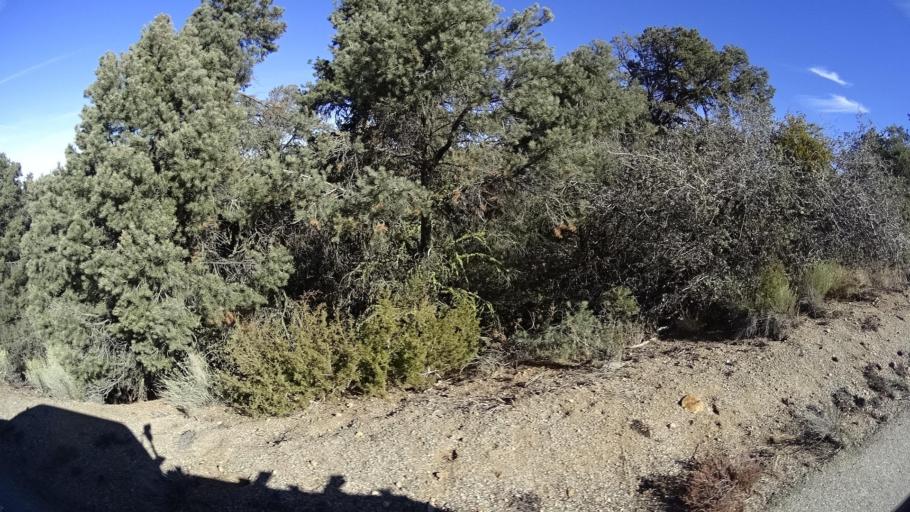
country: US
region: California
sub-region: Kern County
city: Pine Mountain Club
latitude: 34.8723
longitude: -119.2971
